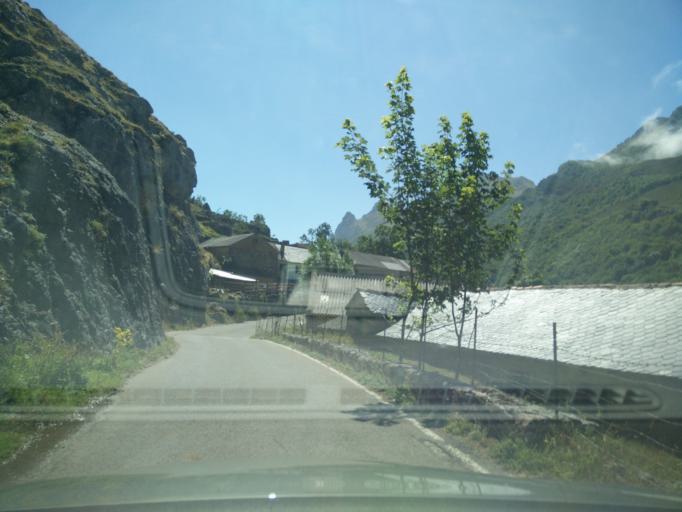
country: ES
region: Asturias
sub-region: Province of Asturias
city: Pola de Somiedo
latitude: 43.0720
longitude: -6.1969
